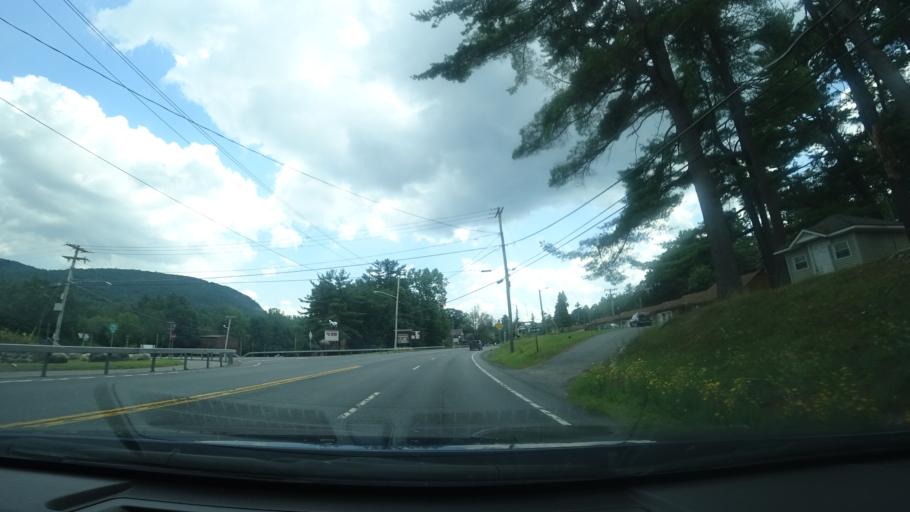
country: US
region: New York
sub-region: Warren County
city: Glens Falls North
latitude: 43.3956
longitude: -73.7039
